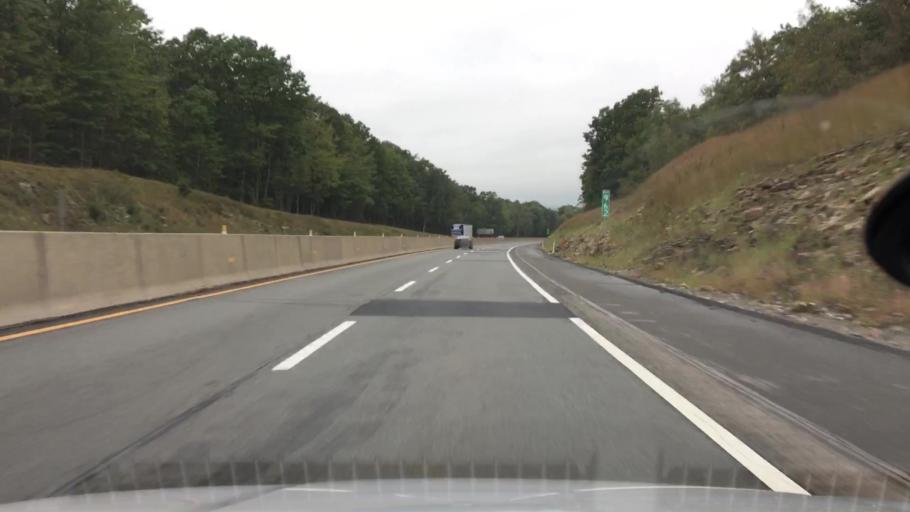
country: US
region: Pennsylvania
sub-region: Luzerne County
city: White Haven
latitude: 41.0806
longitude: -75.7325
